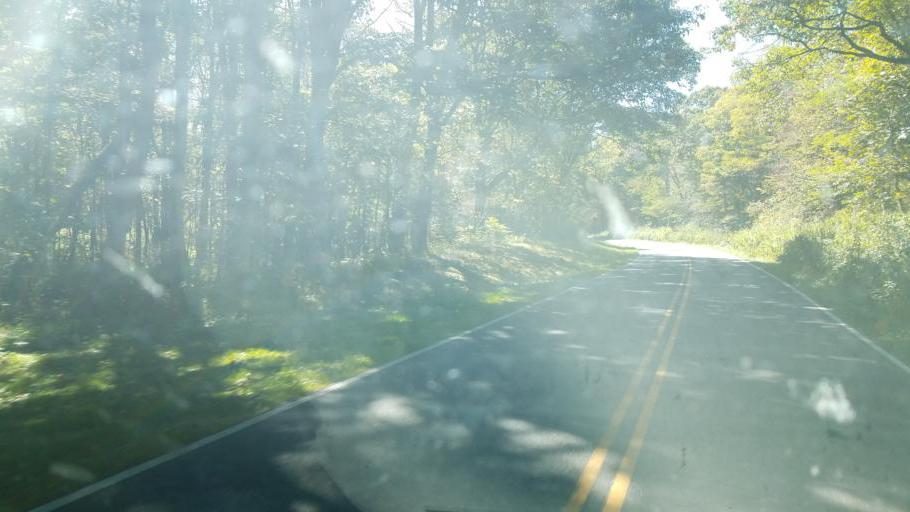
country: US
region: Virginia
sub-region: Greene County
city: Stanardsville
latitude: 38.4147
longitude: -78.4887
